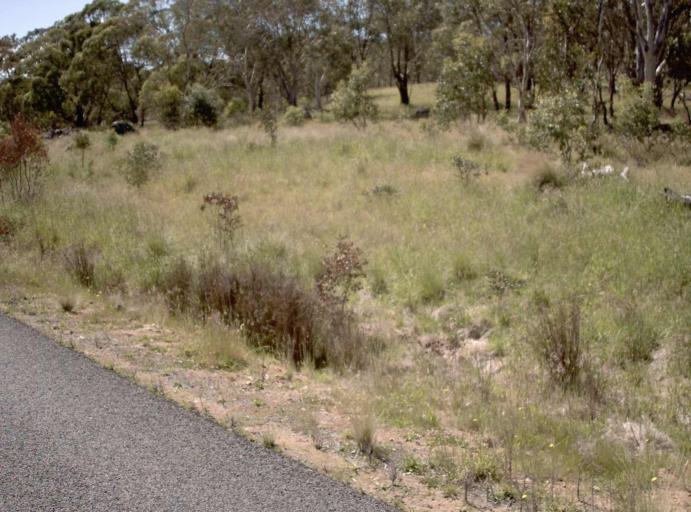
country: AU
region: New South Wales
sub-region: Bombala
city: Bombala
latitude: -37.0439
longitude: 148.8153
